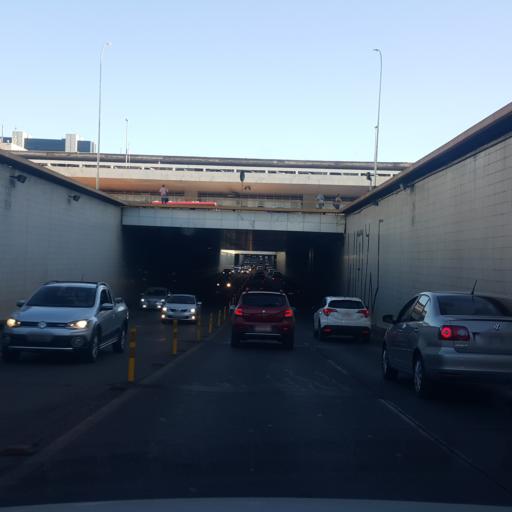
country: BR
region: Federal District
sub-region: Brasilia
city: Brasilia
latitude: -15.7922
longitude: -47.8822
